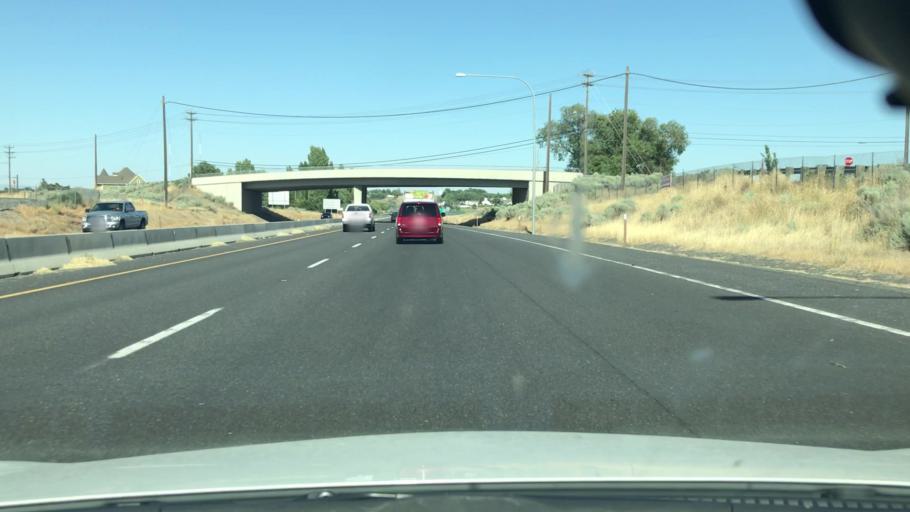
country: US
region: Washington
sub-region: Grant County
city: Cascade Valley
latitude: 47.1006
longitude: -119.3080
